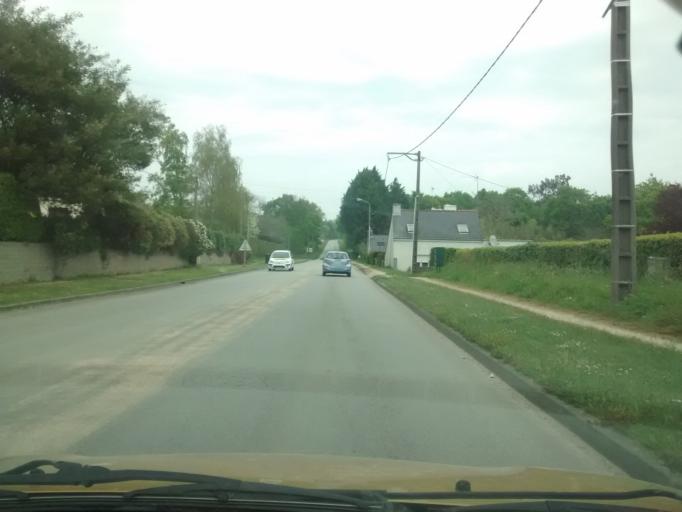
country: FR
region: Brittany
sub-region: Departement du Morbihan
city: Berric
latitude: 47.6344
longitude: -2.5159
